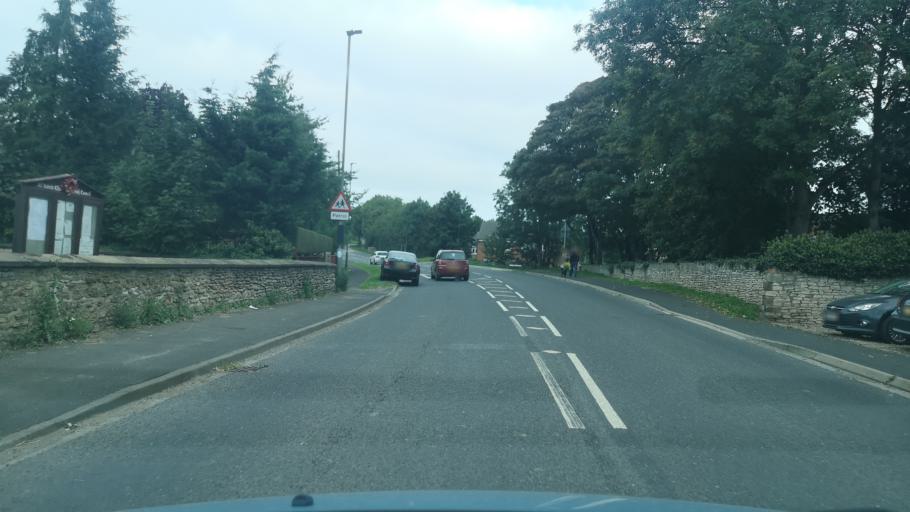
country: GB
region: England
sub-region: Doncaster
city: Norton
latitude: 53.6907
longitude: -1.1542
